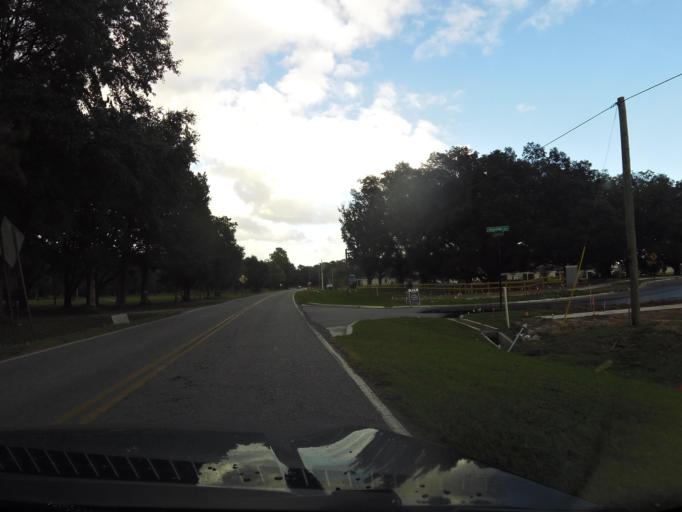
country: US
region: Florida
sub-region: Clay County
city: Asbury Lake
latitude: 30.0479
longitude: -81.7721
